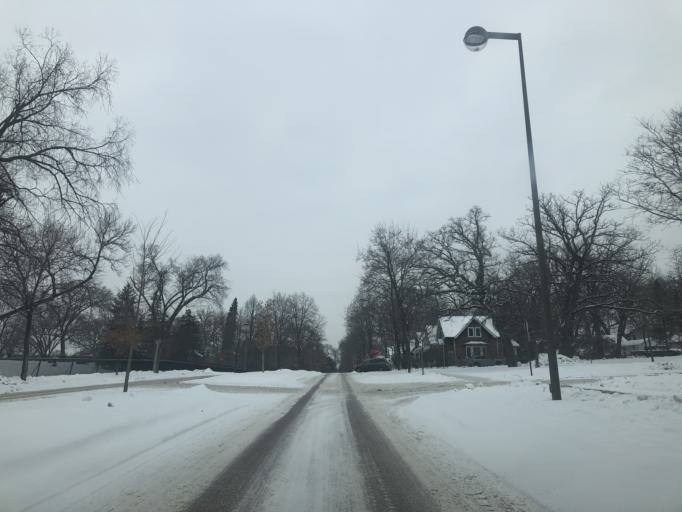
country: US
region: Minnesota
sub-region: Hennepin County
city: Richfield
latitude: 44.9335
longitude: -93.2933
